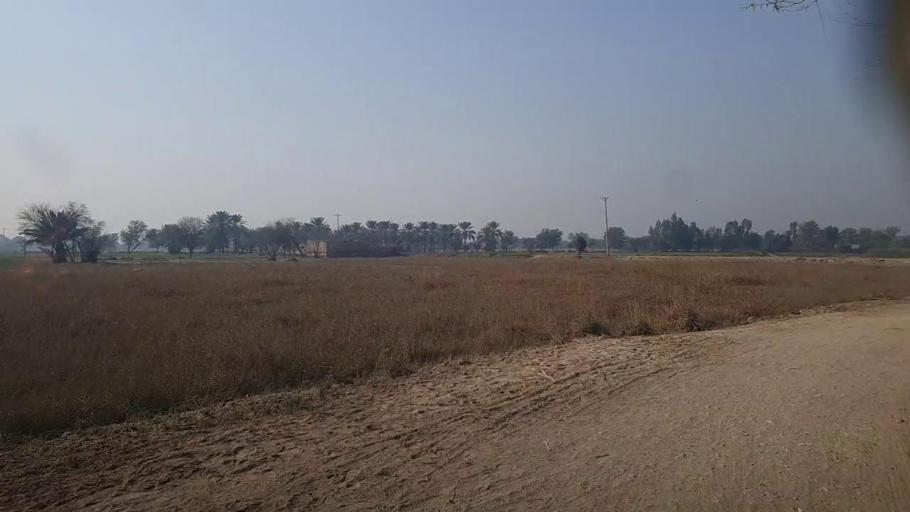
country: PK
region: Sindh
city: Karaundi
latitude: 26.8460
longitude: 68.3884
